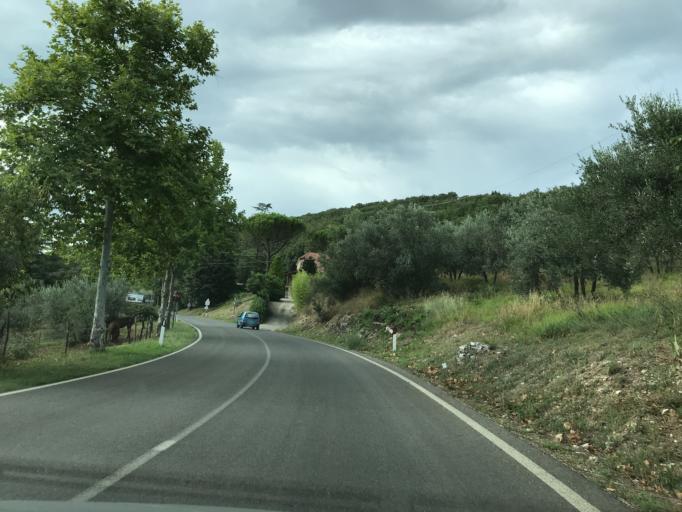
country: IT
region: Umbria
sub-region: Provincia di Terni
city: Guardea
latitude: 42.6301
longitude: 12.2964
